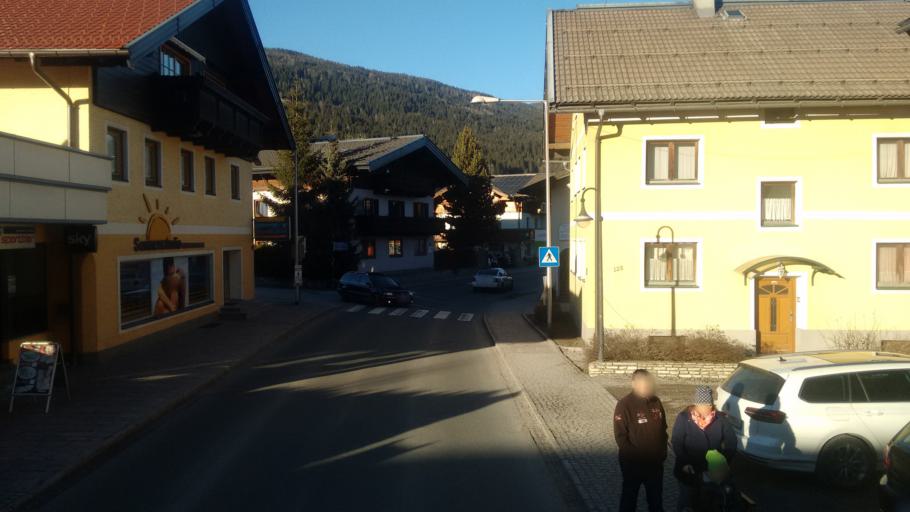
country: AT
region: Salzburg
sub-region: Politischer Bezirk Sankt Johann im Pongau
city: Altenmarkt im Pongau
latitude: 47.3789
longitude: 13.4236
